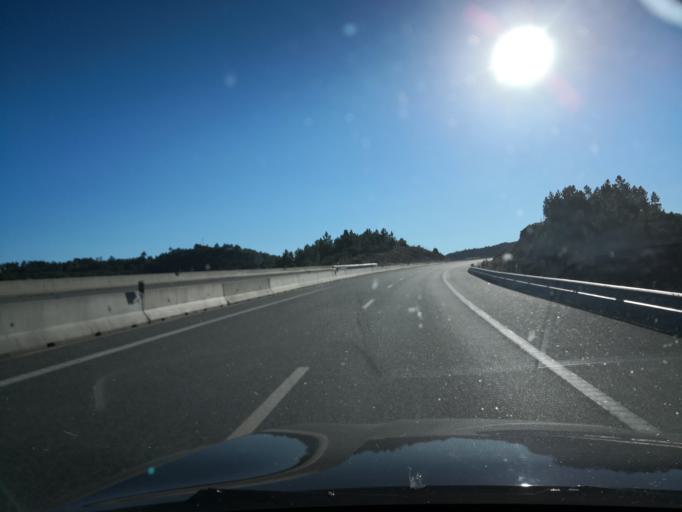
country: PT
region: Vila Real
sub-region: Murca
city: Murca
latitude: 41.3805
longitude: -7.4835
